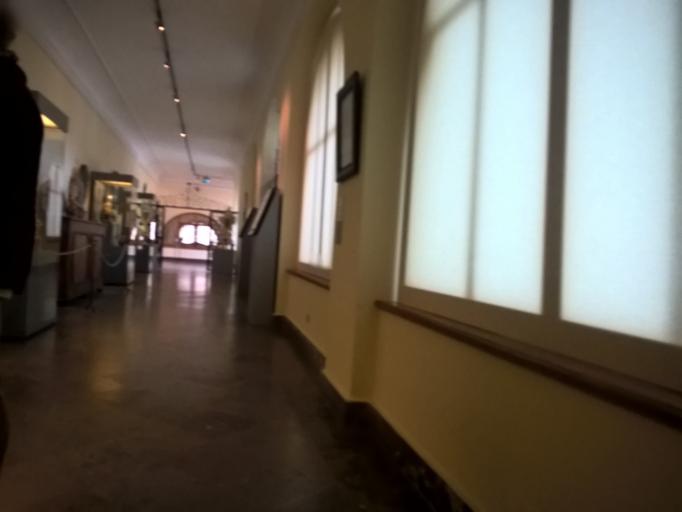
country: CZ
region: Praha
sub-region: Praha 1
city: Mala Strana
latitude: 50.0891
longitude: 14.3920
